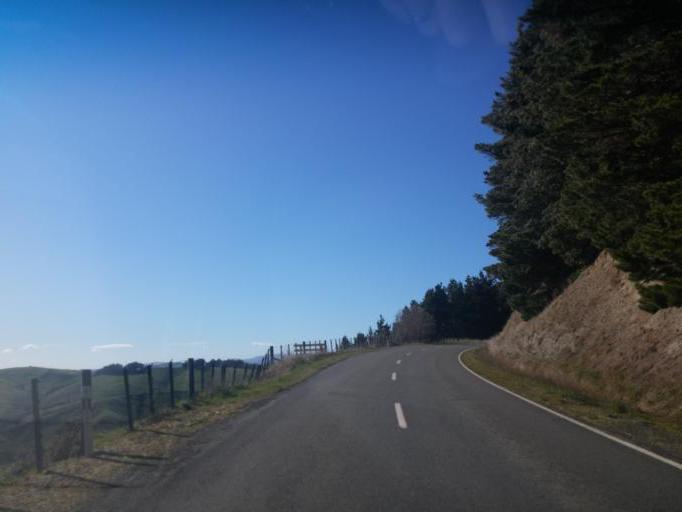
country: NZ
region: Wellington
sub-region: South Wairarapa District
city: Waipawa
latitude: -41.3493
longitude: 175.4884
